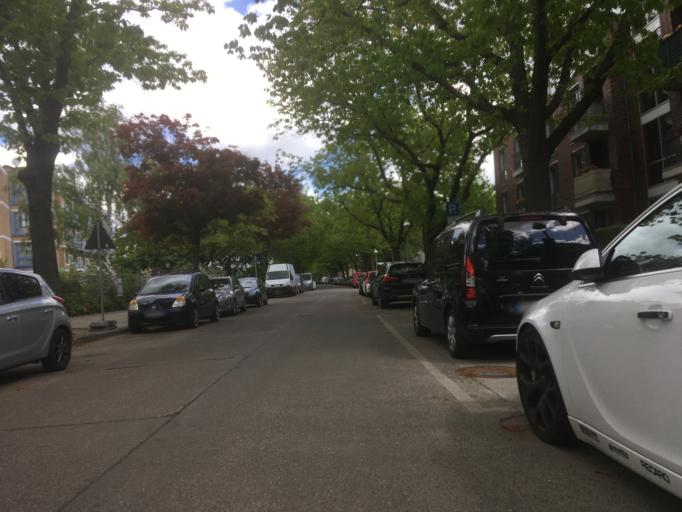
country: DE
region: Berlin
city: Tempelhof Bezirk
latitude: 52.4614
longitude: 13.3944
